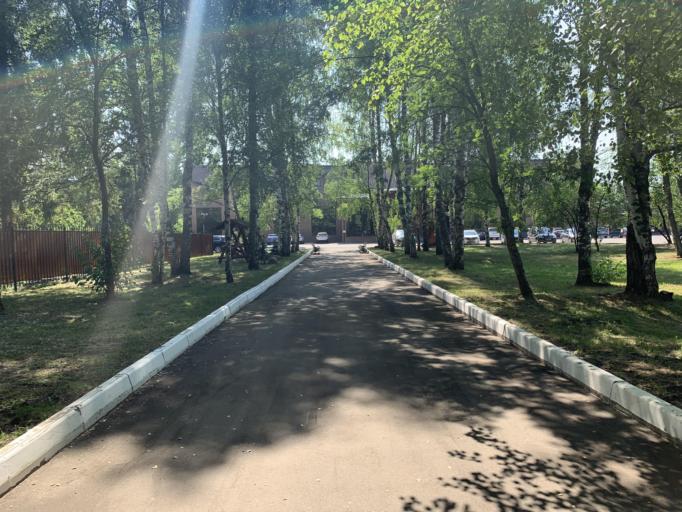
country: RU
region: Kostroma
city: Oktyabr'skiy
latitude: 57.6419
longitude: 41.0917
